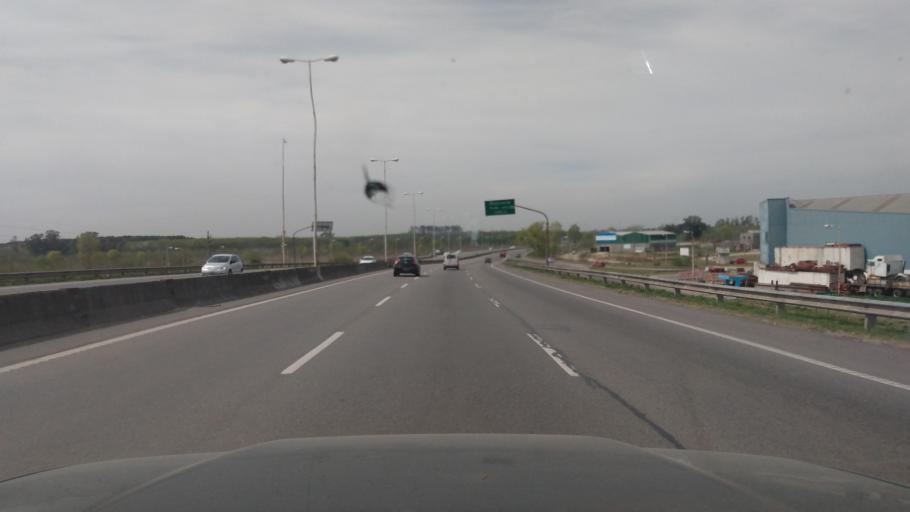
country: AR
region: Buenos Aires
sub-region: Partido de Pilar
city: Pilar
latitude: -34.4405
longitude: -58.9689
